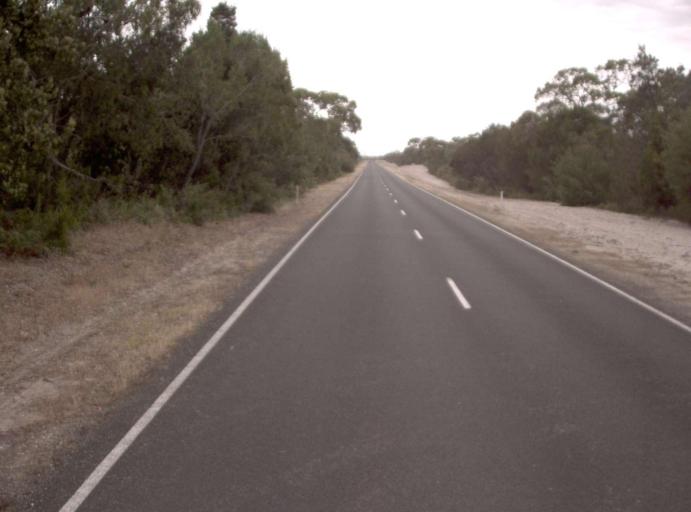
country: AU
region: Victoria
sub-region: Wellington
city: Sale
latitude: -38.1788
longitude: 147.3788
